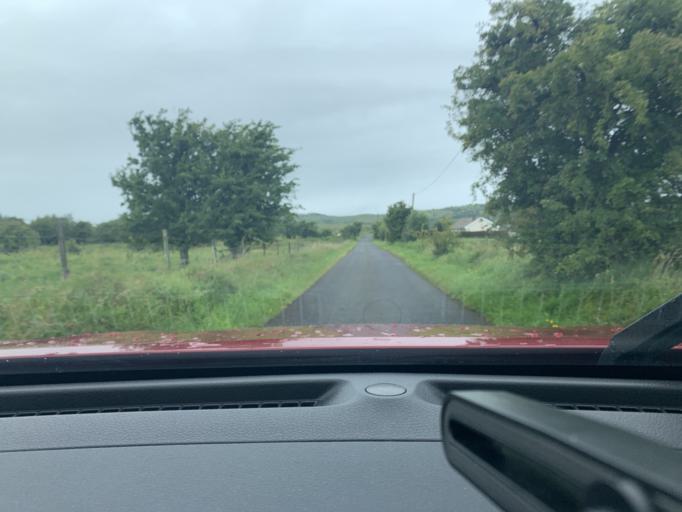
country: GB
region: Northern Ireland
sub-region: Fermanagh District
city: Enniskillen
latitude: 54.2580
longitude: -7.8453
